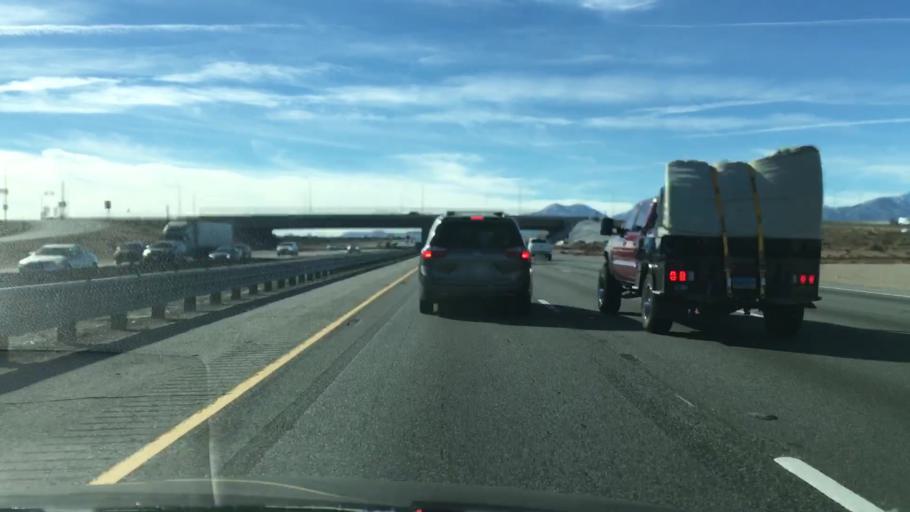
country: US
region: California
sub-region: San Bernardino County
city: Oak Hills
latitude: 34.3853
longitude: -117.4136
